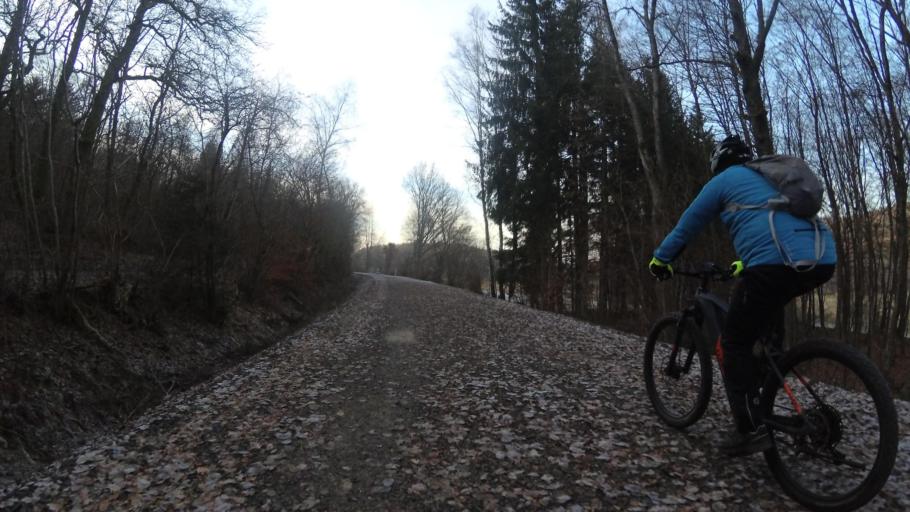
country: DE
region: Saarland
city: Nohfelden
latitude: 49.5754
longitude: 7.1581
